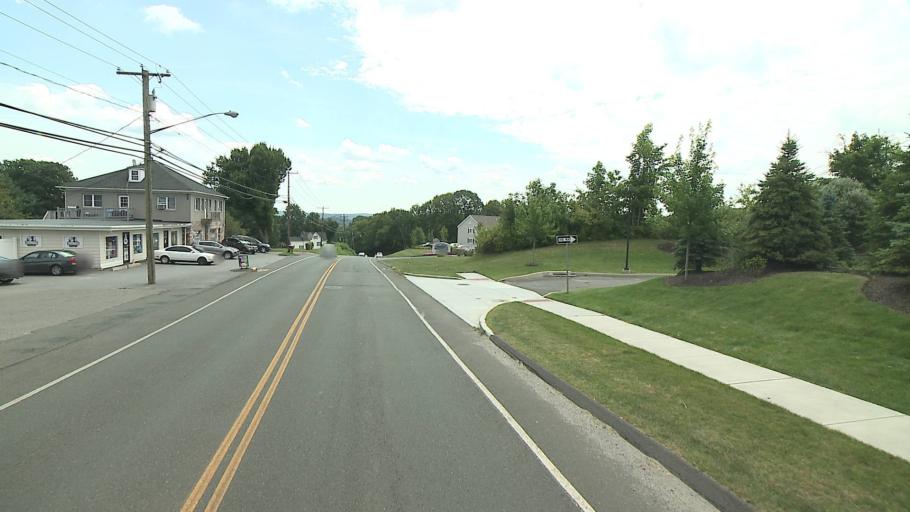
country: US
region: Connecticut
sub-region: Fairfield County
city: Danbury
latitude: 41.4067
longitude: -73.4664
